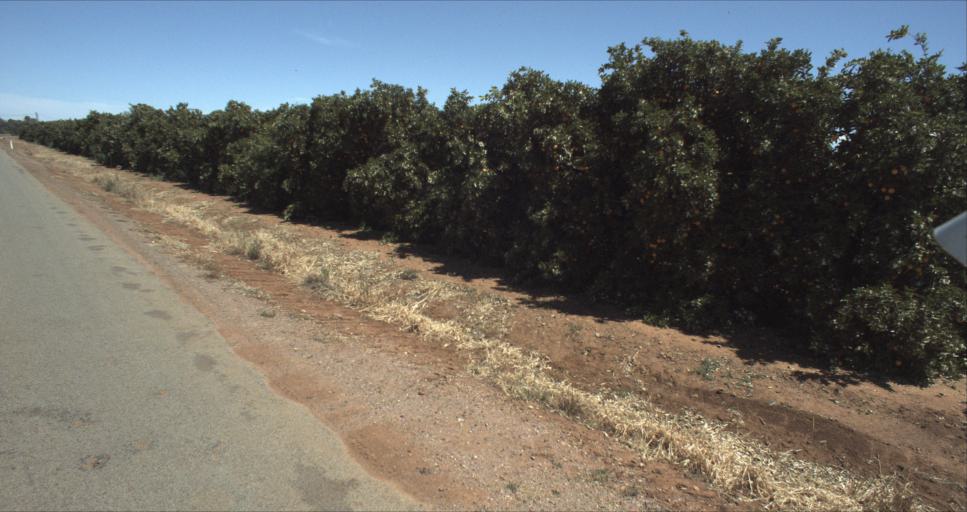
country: AU
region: New South Wales
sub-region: Leeton
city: Leeton
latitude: -34.5323
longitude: 146.3288
